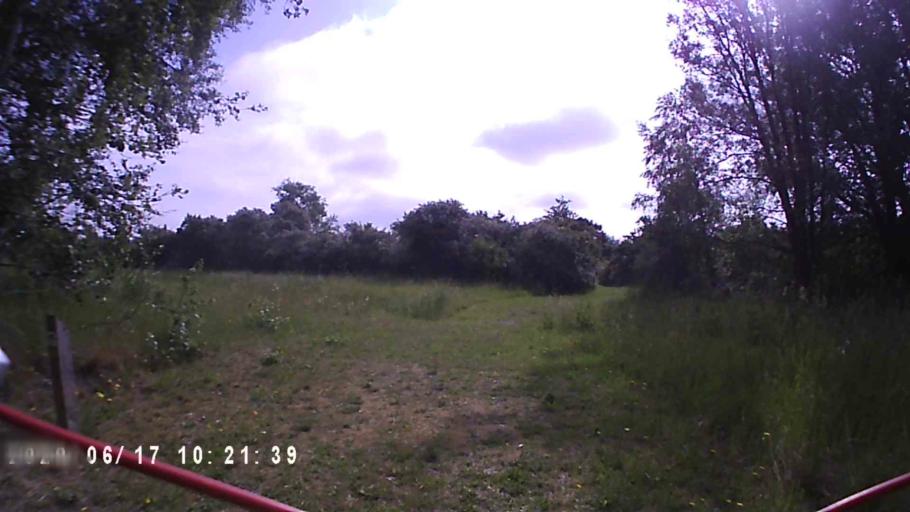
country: NL
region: Groningen
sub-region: Gemeente De Marne
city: Ulrum
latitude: 53.3908
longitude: 6.2506
